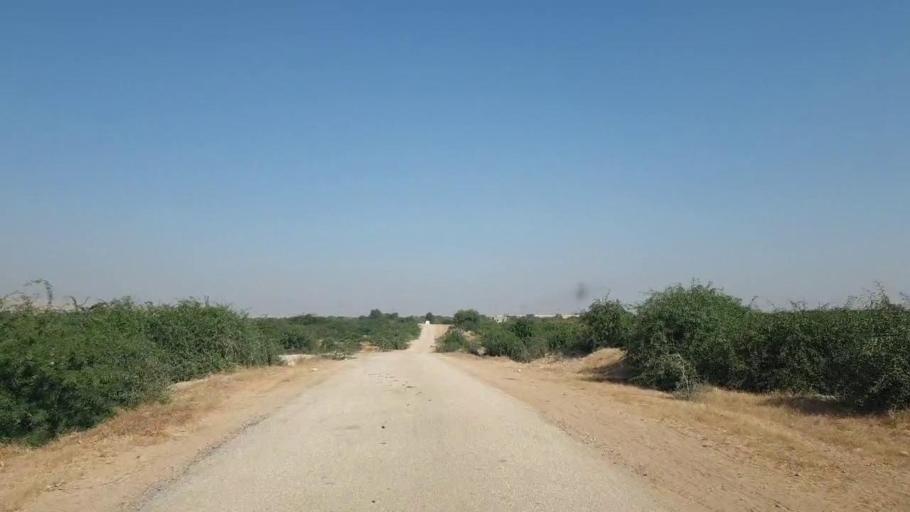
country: PK
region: Sindh
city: Gharo
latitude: 25.1768
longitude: 67.7339
